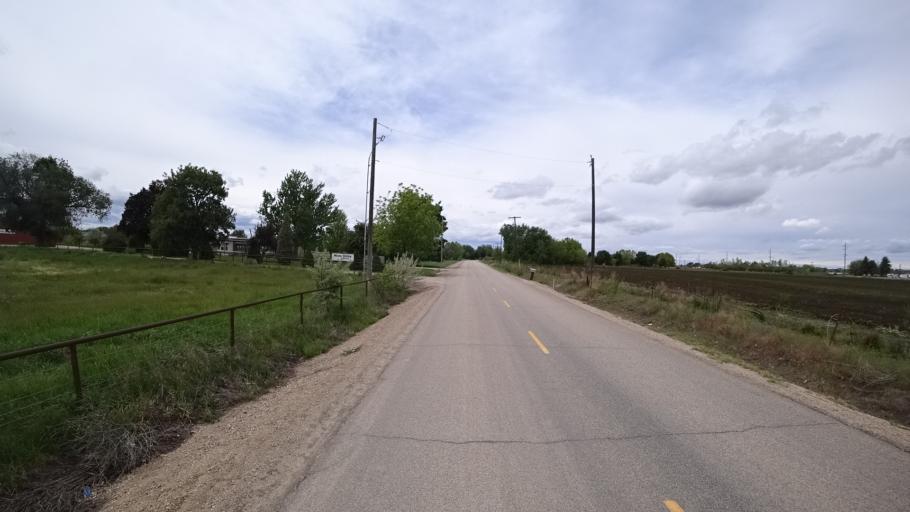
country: US
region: Idaho
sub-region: Ada County
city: Star
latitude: 43.6898
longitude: -116.4355
